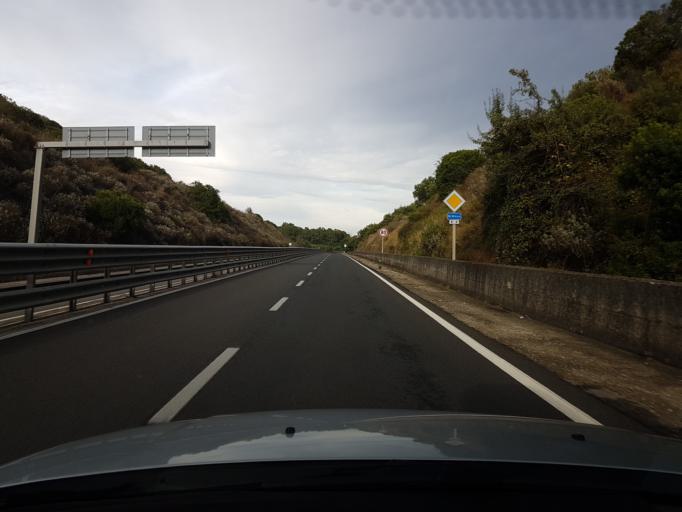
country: IT
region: Sardinia
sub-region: Provincia di Oristano
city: Soddi
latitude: 40.1481
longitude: 8.8847
